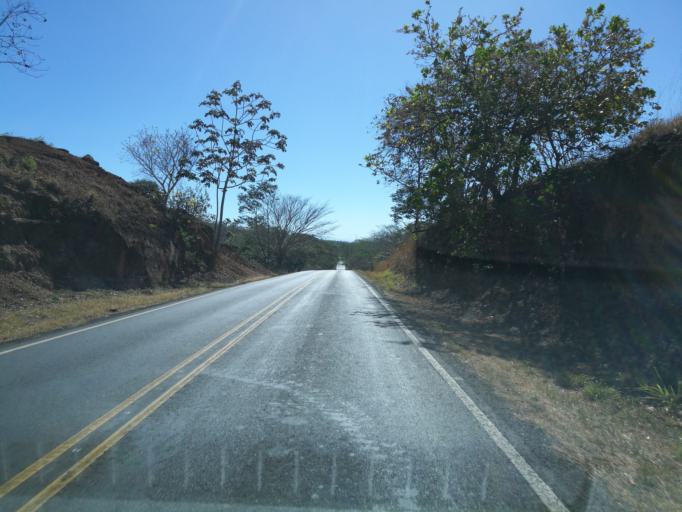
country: CR
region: Puntarenas
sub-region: Canton Central de Puntarenas
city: Puntarenas
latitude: 10.0988
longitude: -84.8652
